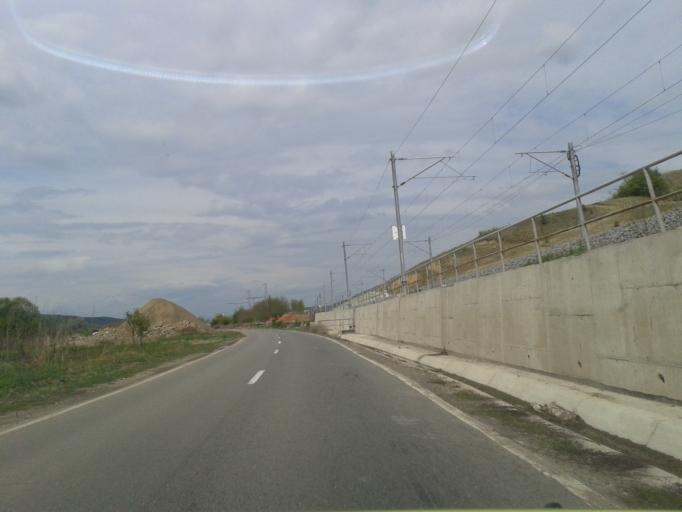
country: RO
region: Alba
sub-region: Comuna Valea Lunga
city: Valea Lunga
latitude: 46.0914
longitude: 24.0651
